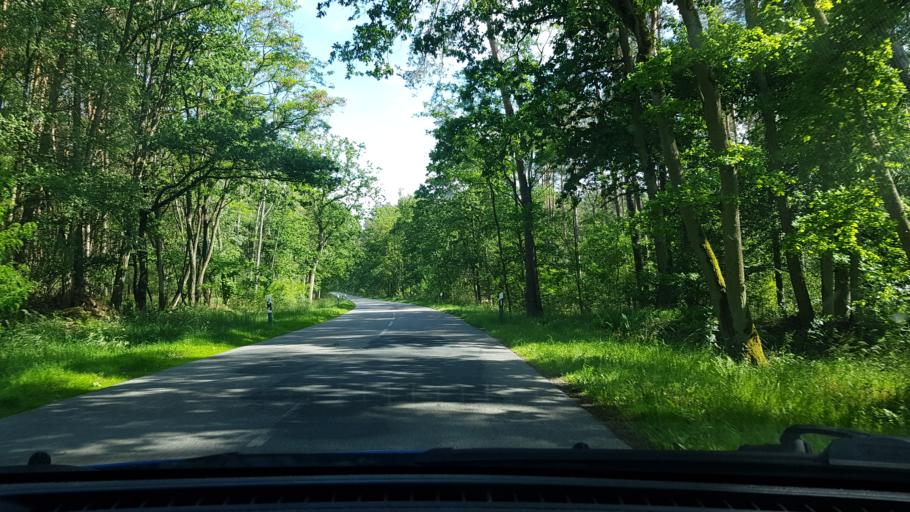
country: DE
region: Lower Saxony
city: Neu Darchau
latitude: 53.3157
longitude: 10.9097
